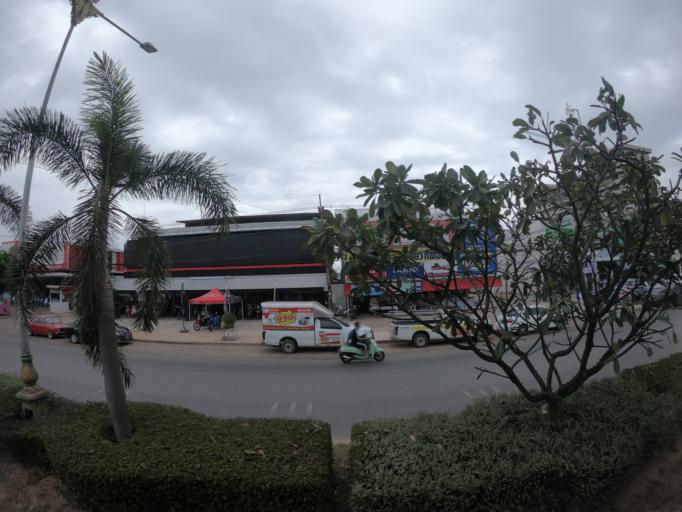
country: TH
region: Maha Sarakham
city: Maha Sarakham
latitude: 16.1799
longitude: 103.2988
